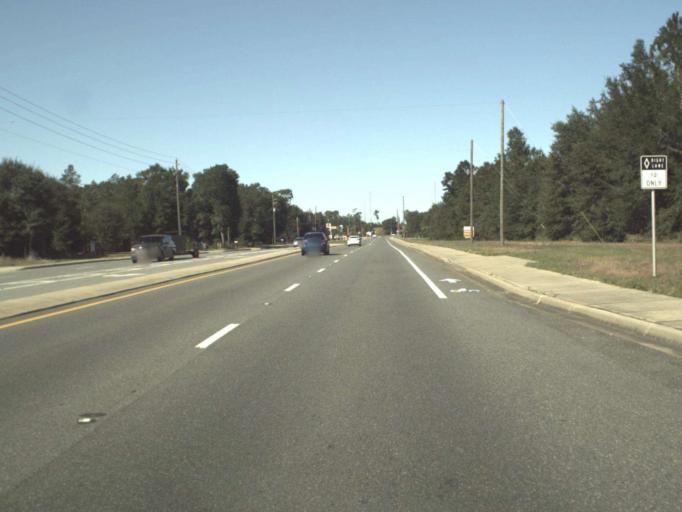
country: US
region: Florida
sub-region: Santa Rosa County
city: East Milton
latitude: 30.6126
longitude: -86.9578
